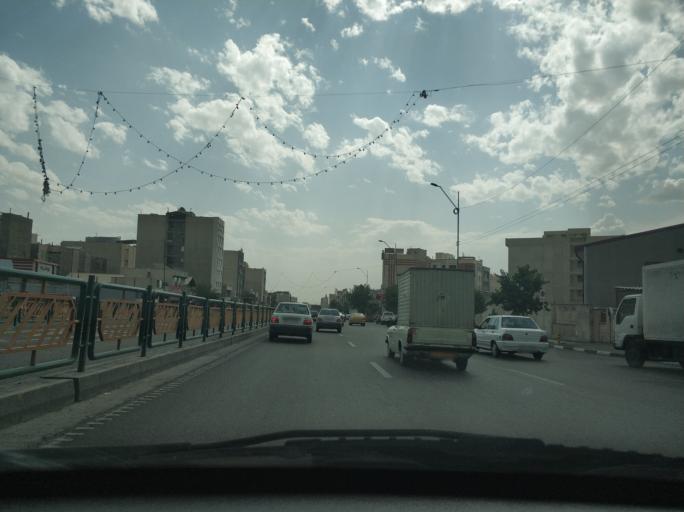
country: IR
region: Tehran
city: Tehran
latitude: 35.7217
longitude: 51.5130
